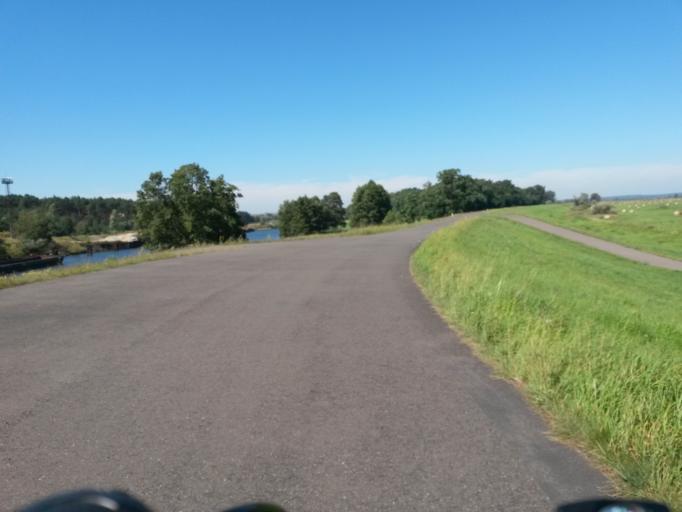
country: PL
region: West Pomeranian Voivodeship
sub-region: Powiat gryfinski
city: Cedynia
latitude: 52.8987
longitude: 14.1504
